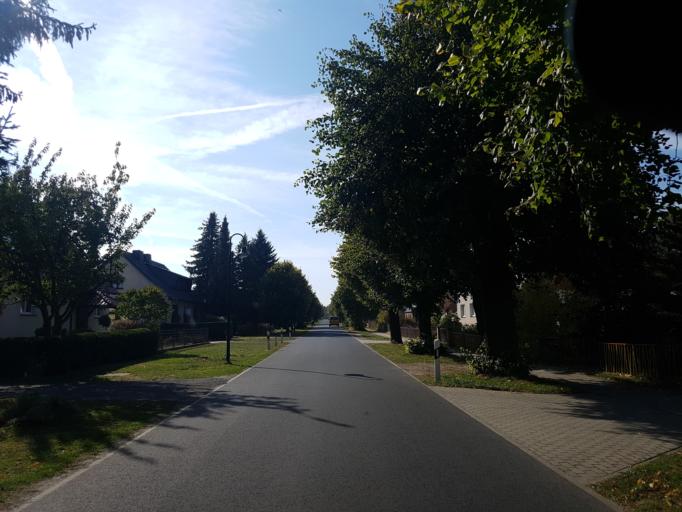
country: DE
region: Brandenburg
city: Hohenbucko
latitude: 51.7635
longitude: 13.4684
